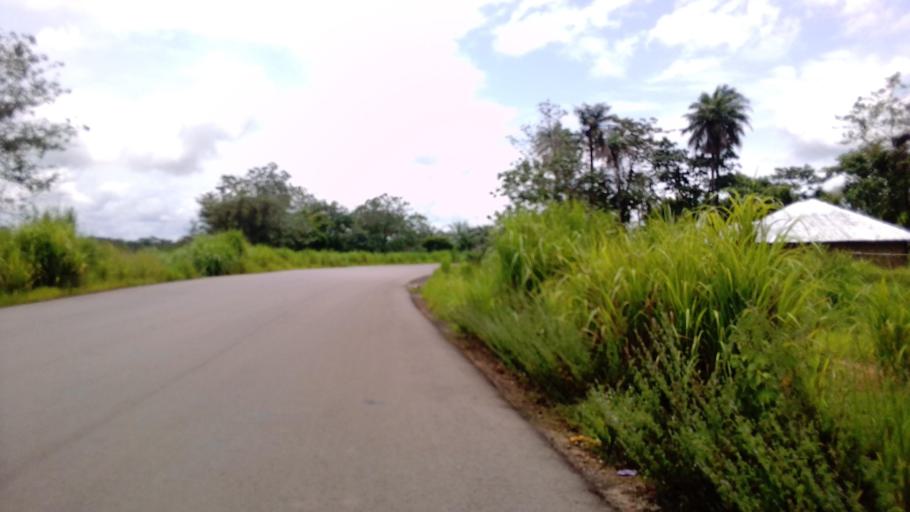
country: SL
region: Northern Province
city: Makeni
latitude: 9.0637
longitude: -12.1767
